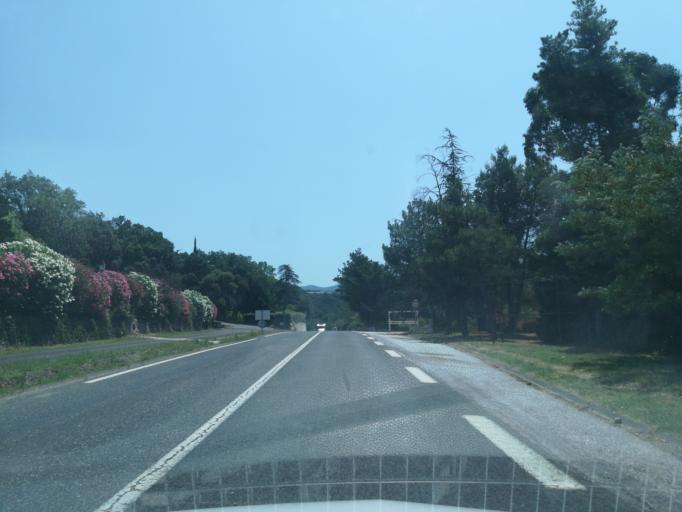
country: FR
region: Languedoc-Roussillon
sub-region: Departement des Pyrenees-Orientales
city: Maureillas-las-Illas
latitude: 42.4907
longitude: 2.8330
